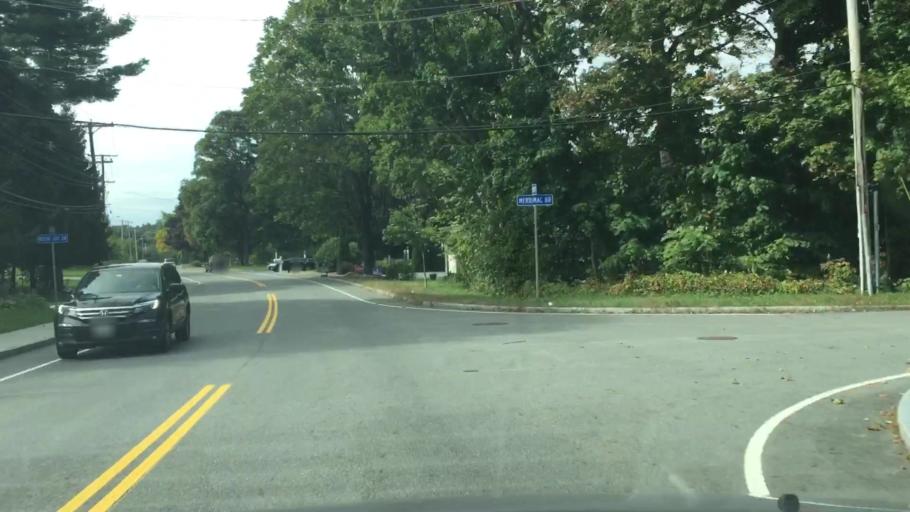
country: US
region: Massachusetts
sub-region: Middlesex County
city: Tewksbury
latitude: 42.6508
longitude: -71.2542
